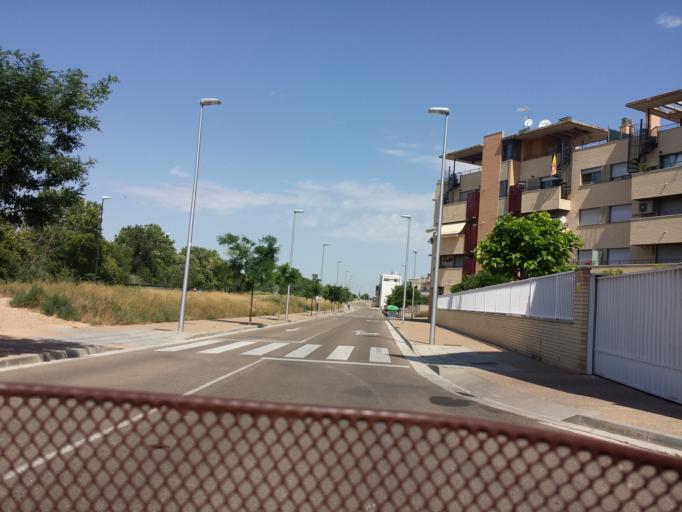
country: ES
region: Aragon
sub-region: Provincia de Zaragoza
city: Montecanal
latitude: 41.6357
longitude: -0.9341
